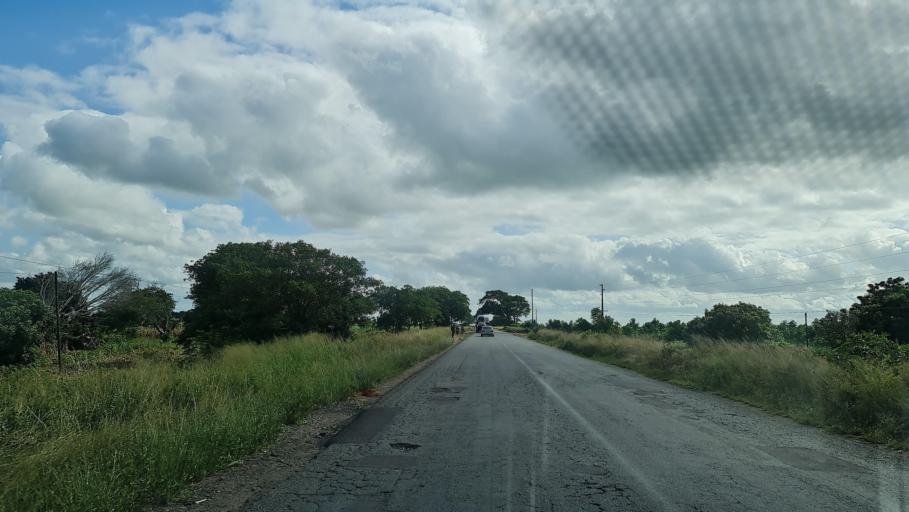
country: MZ
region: Gaza
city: Macia
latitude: -25.0873
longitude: 32.8441
